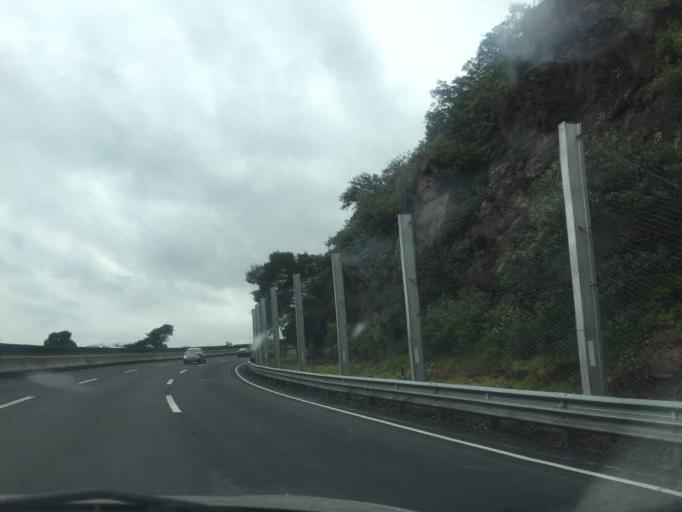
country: MX
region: Mexico City
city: Xochimilco
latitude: 19.2252
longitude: -99.1364
